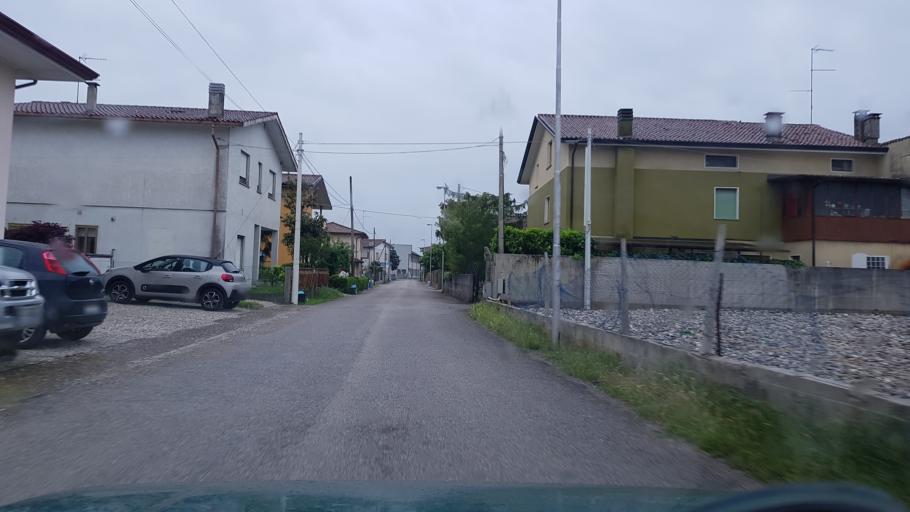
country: IT
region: Friuli Venezia Giulia
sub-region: Provincia di Udine
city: San Giovanni al Natisone
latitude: 45.9739
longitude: 13.3996
